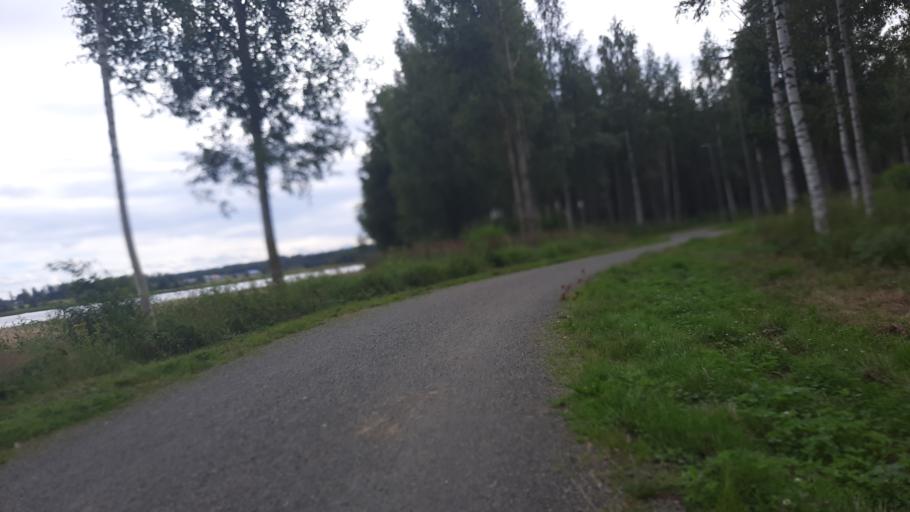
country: FI
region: North Karelia
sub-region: Joensuu
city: Joensuu
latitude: 62.6144
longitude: 29.8557
